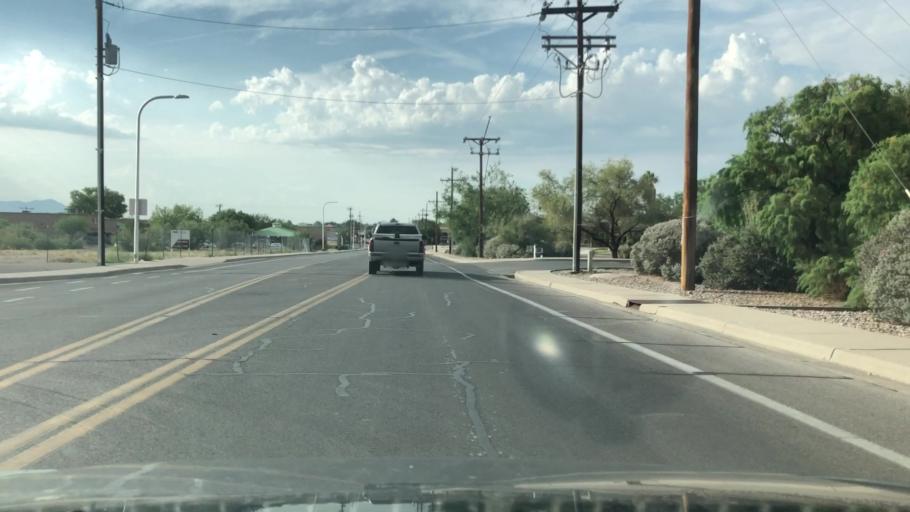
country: US
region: New Mexico
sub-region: Dona Ana County
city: University Park
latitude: 32.2863
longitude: -106.7476
